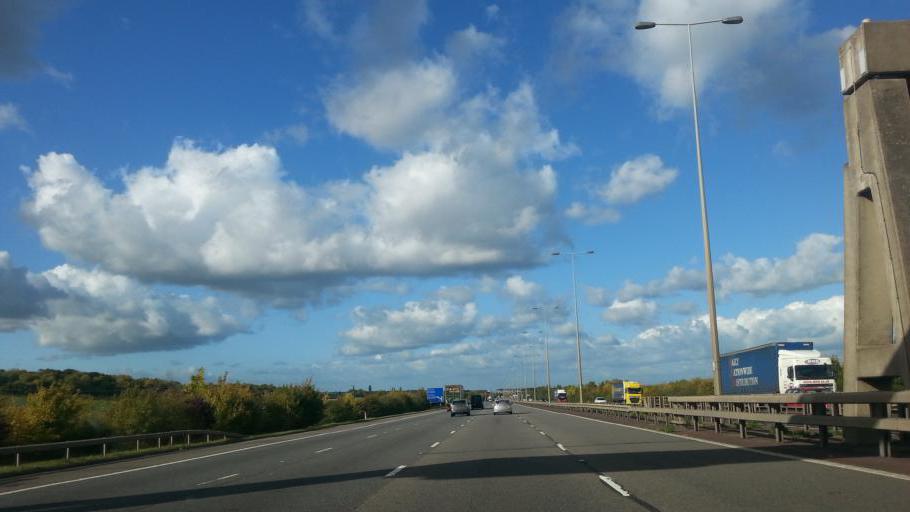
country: GB
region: England
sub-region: Cambridgeshire
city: Sawtry
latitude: 52.4086
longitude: -0.2650
